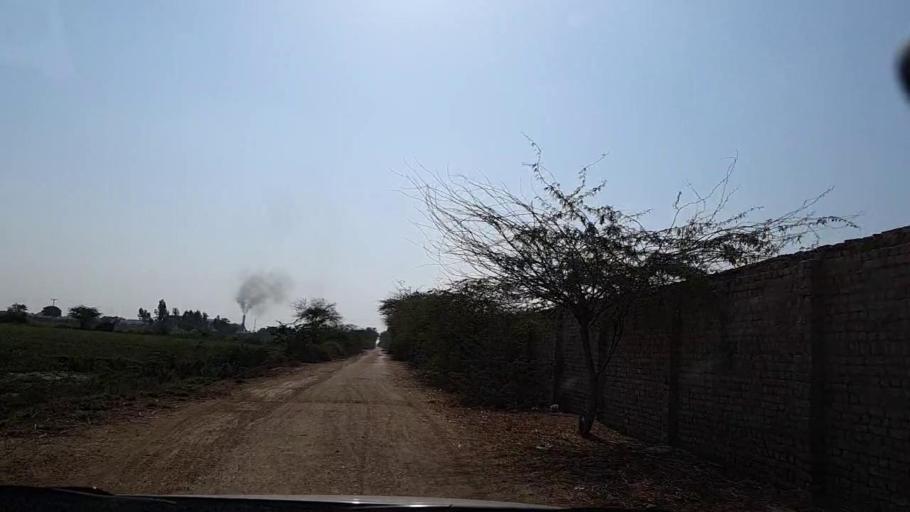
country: PK
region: Sindh
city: Digri
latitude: 25.1714
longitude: 69.0426
